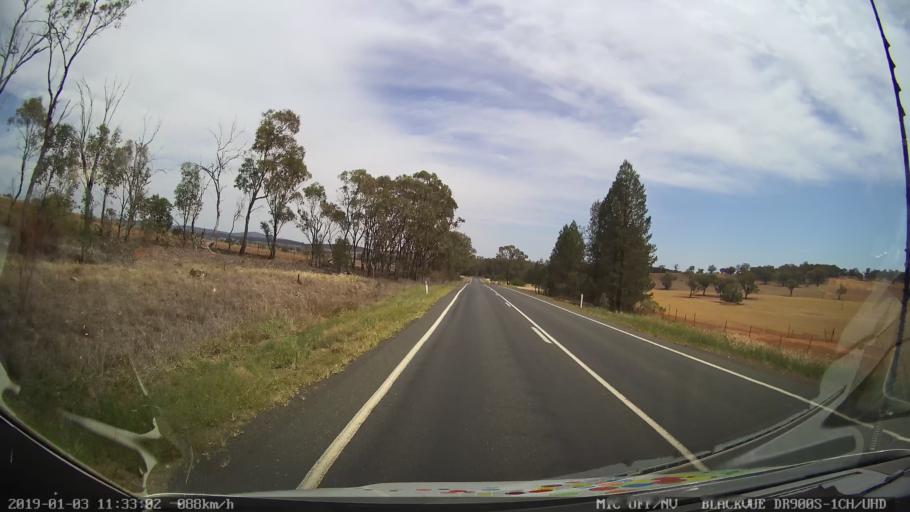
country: AU
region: New South Wales
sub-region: Weddin
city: Grenfell
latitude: -33.9512
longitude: 148.1749
